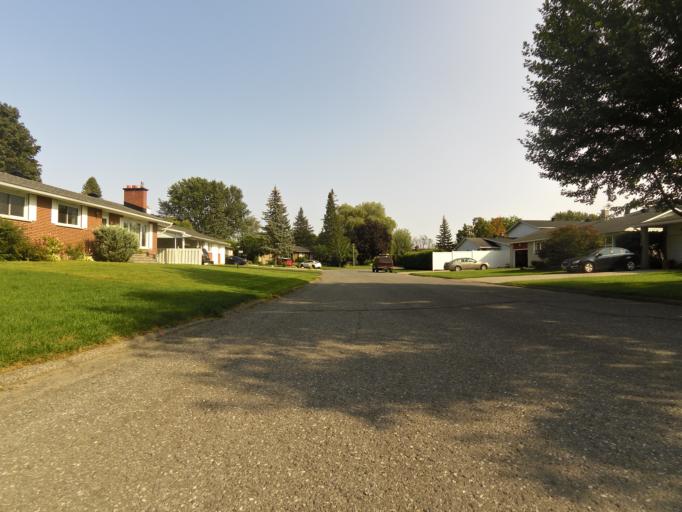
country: CA
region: Ontario
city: Bells Corners
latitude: 45.2971
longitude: -75.8819
